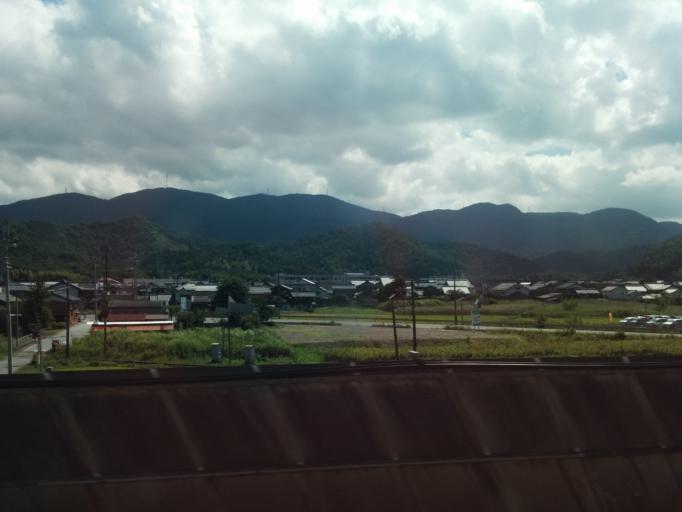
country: JP
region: Shiga Prefecture
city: Hikone
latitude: 35.2828
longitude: 136.2809
